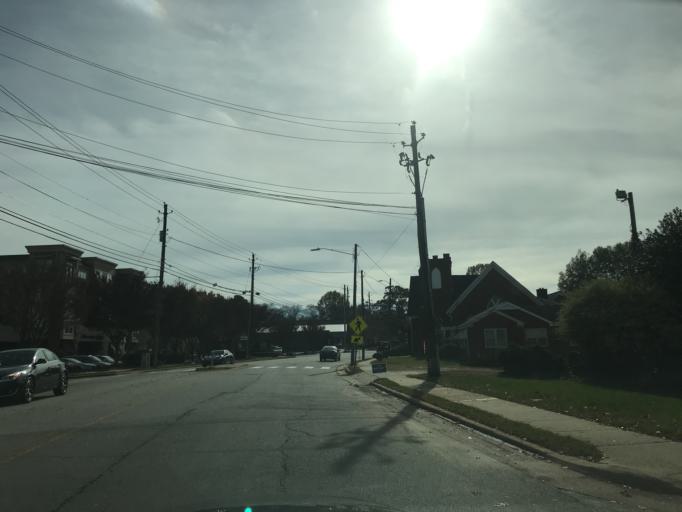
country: US
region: North Carolina
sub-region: Wake County
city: West Raleigh
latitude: 35.7984
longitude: -78.6602
